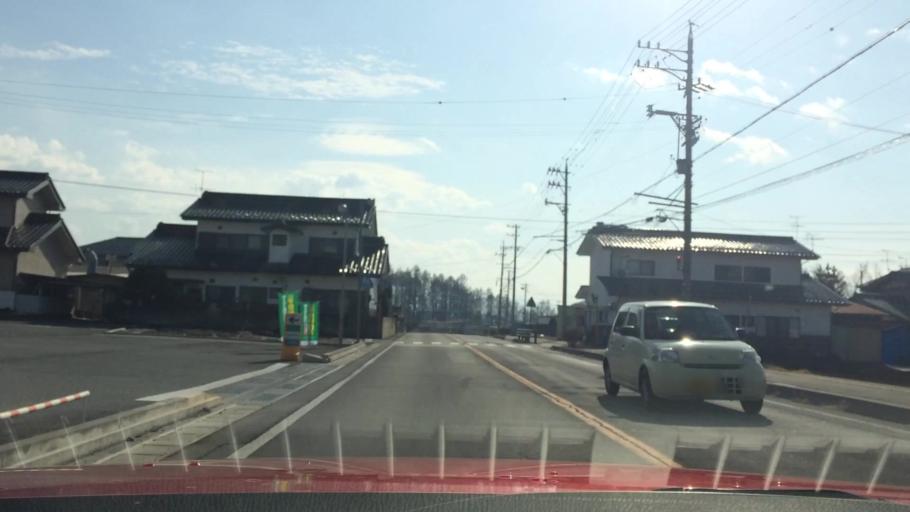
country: JP
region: Nagano
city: Komoro
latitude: 36.2987
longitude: 138.4930
